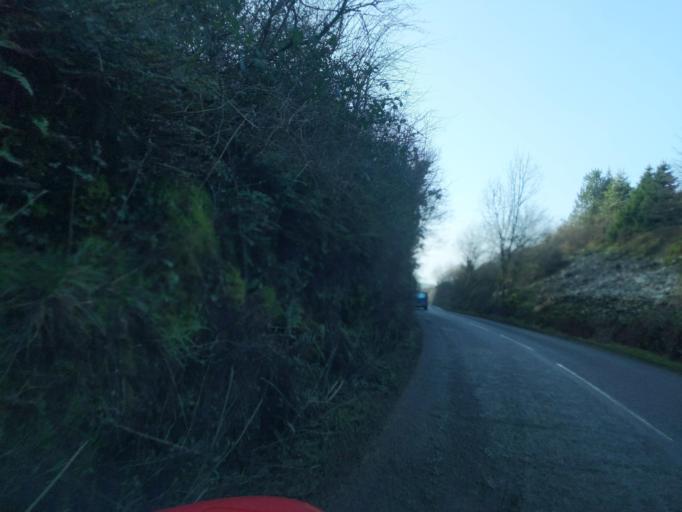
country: GB
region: England
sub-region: Cornwall
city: Tintagel
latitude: 50.6433
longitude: -4.7173
